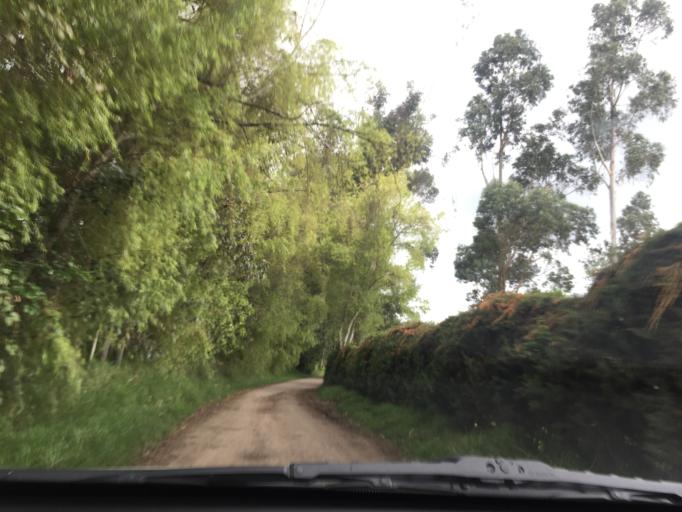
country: CO
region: Cundinamarca
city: Subachoque
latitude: 4.9483
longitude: -74.1411
